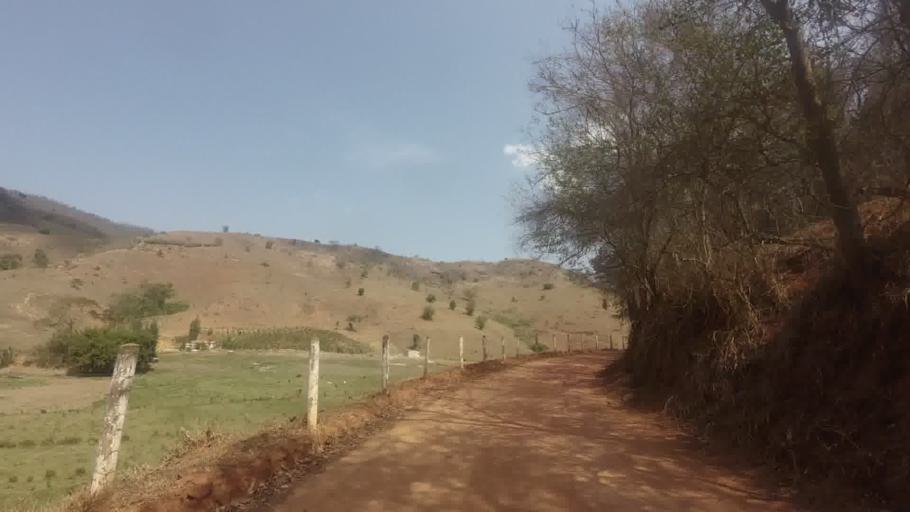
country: BR
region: Espirito Santo
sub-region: Sao Jose Do Calcado
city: Sao Jose do Calcado
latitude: -21.0531
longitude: -41.5302
